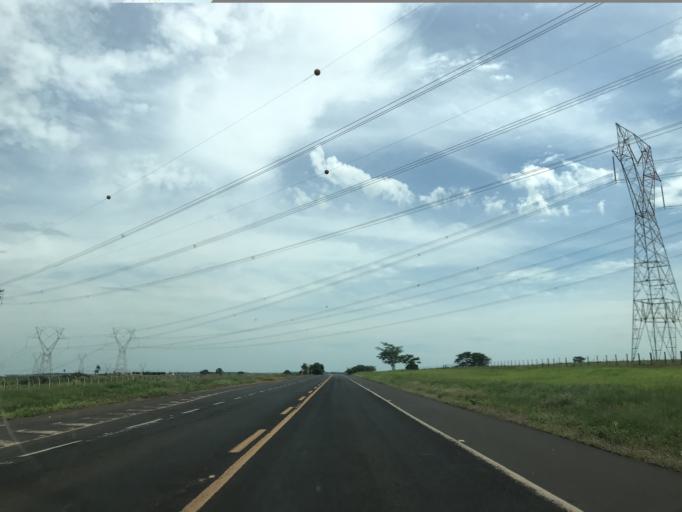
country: BR
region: Sao Paulo
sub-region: Nova Granada
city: Nova Granada
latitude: -20.3372
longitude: -49.2143
